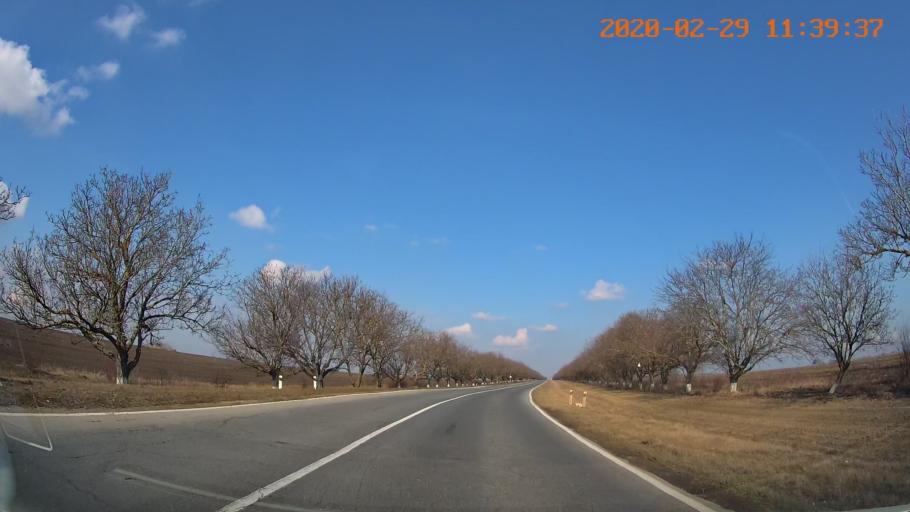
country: MD
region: Rezina
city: Saharna
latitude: 47.6433
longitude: 29.0239
